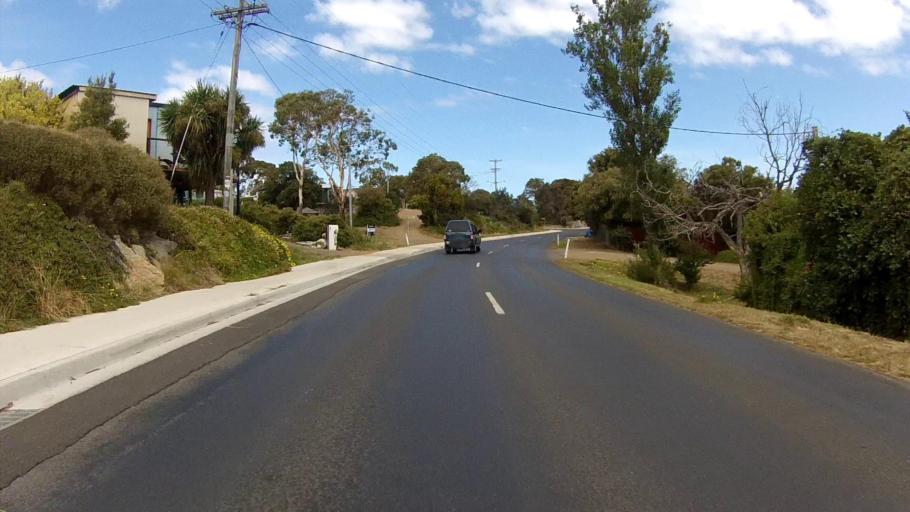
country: AU
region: Tasmania
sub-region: Sorell
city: Sorell
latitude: -42.8610
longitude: 147.6126
